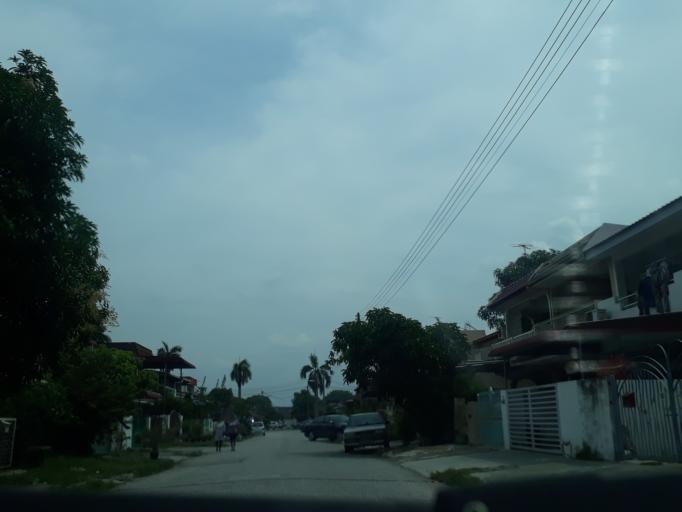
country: MY
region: Perak
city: Ipoh
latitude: 4.5931
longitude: 101.1322
